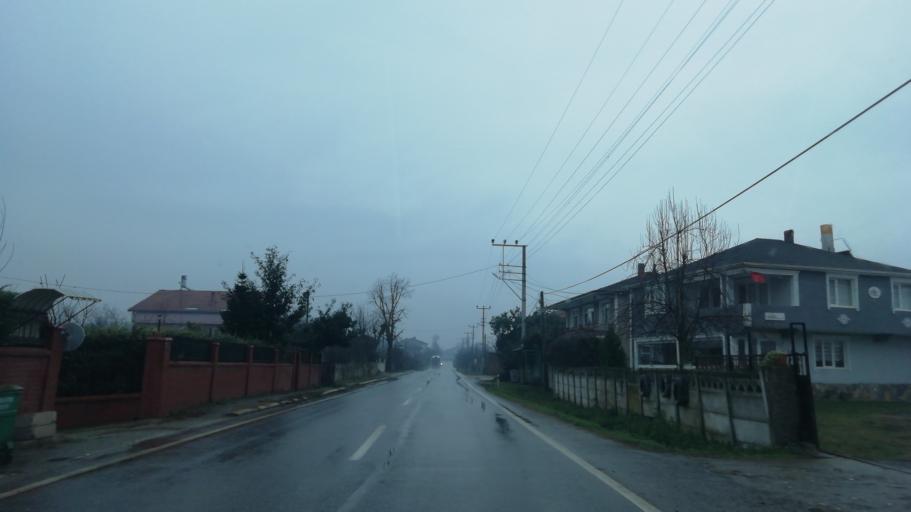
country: TR
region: Sakarya
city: Karapurcek
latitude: 40.6830
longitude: 30.5299
